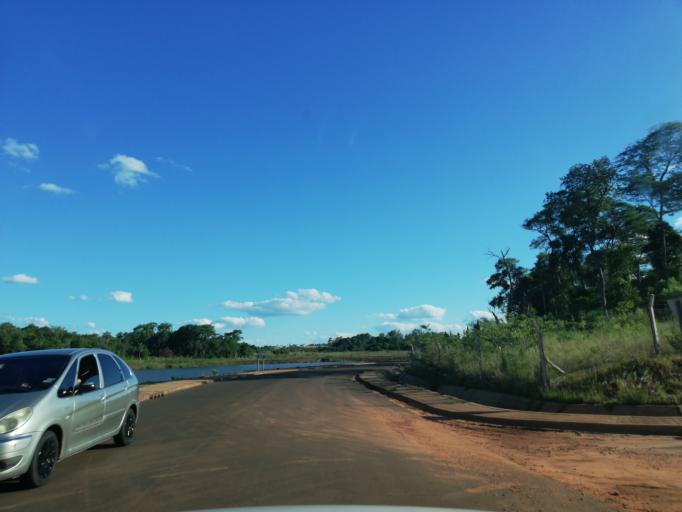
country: AR
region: Misiones
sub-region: Departamento de Candelaria
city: Candelaria
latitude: -27.4506
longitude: -55.7746
